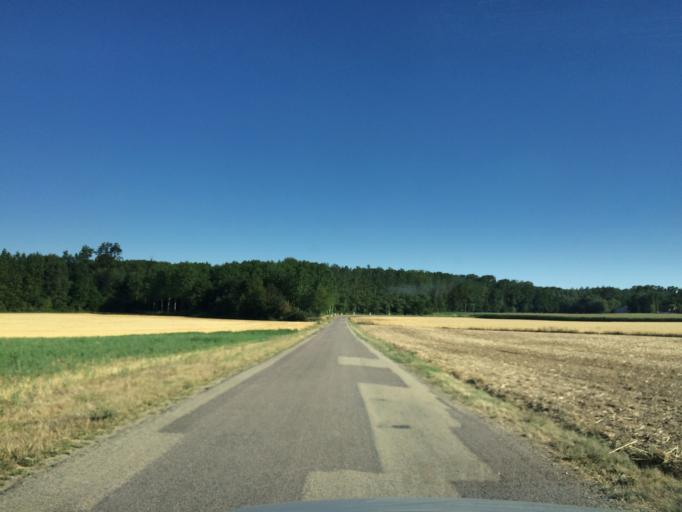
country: FR
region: Bourgogne
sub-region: Departement de l'Yonne
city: Fleury-la-Vallee
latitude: 47.9088
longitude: 3.4414
